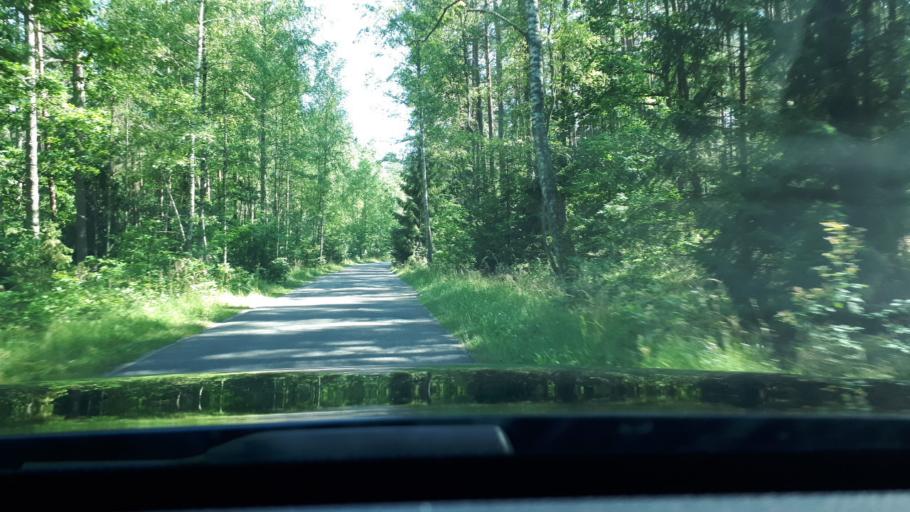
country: PL
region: Warmian-Masurian Voivodeship
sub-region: Powiat olsztynski
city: Stawiguda
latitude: 53.5776
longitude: 20.4546
